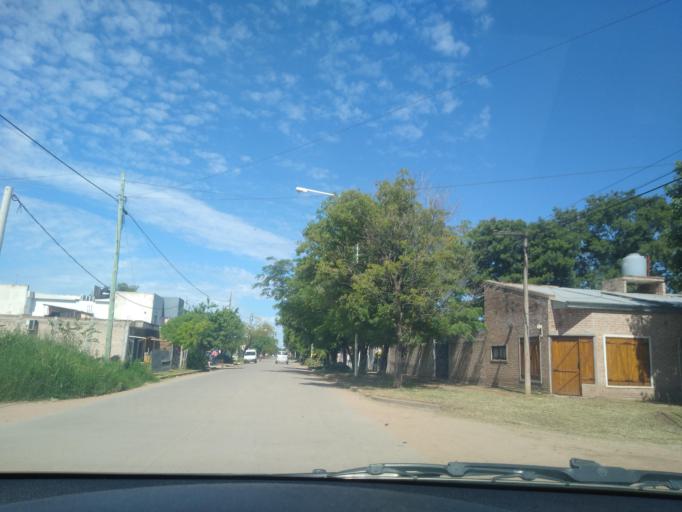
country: AR
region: Chaco
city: Presidencia Roque Saenz Pena
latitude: -26.7761
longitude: -60.4247
